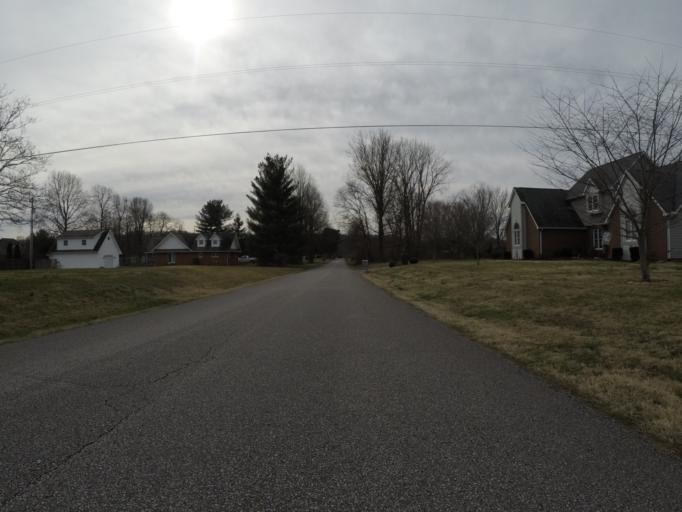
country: US
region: West Virginia
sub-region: Cabell County
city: Pea Ridge
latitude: 38.4498
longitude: -82.3504
